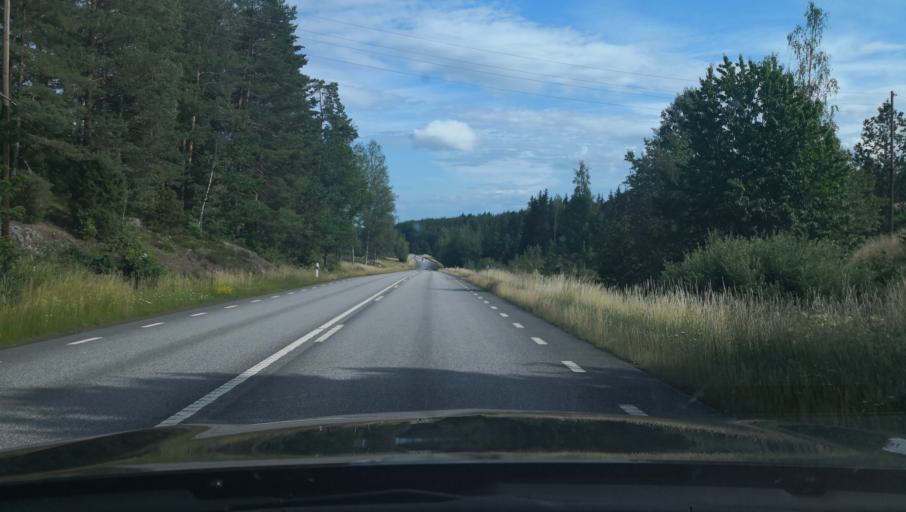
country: SE
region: OEstergoetland
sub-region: Kinda Kommun
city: Kisa
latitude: 57.9177
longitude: 15.6824
